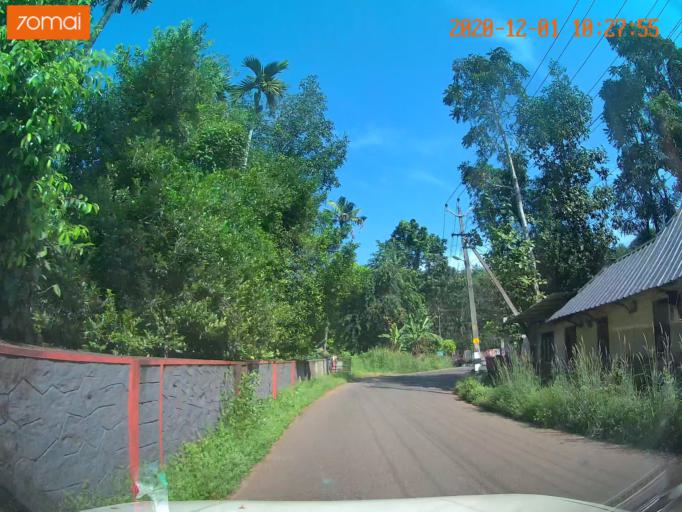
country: IN
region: Kerala
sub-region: Ernakulam
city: Ramamangalam
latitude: 9.9335
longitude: 76.5221
